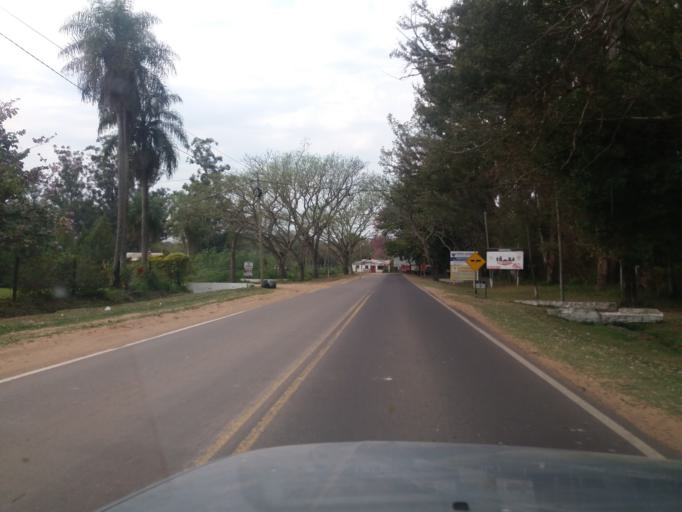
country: AR
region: Corrientes
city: San Luis del Palmar
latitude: -27.4597
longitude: -58.6624
